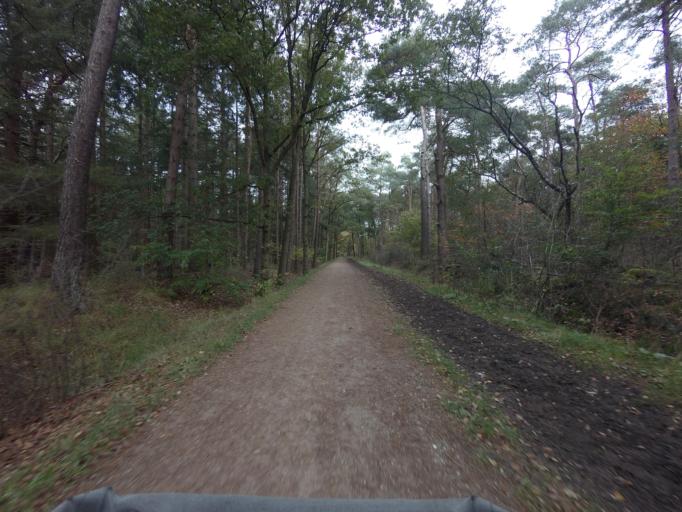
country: NL
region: North Holland
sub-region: Gemeente Hilversum
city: Hilversum
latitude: 52.1847
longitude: 5.1985
